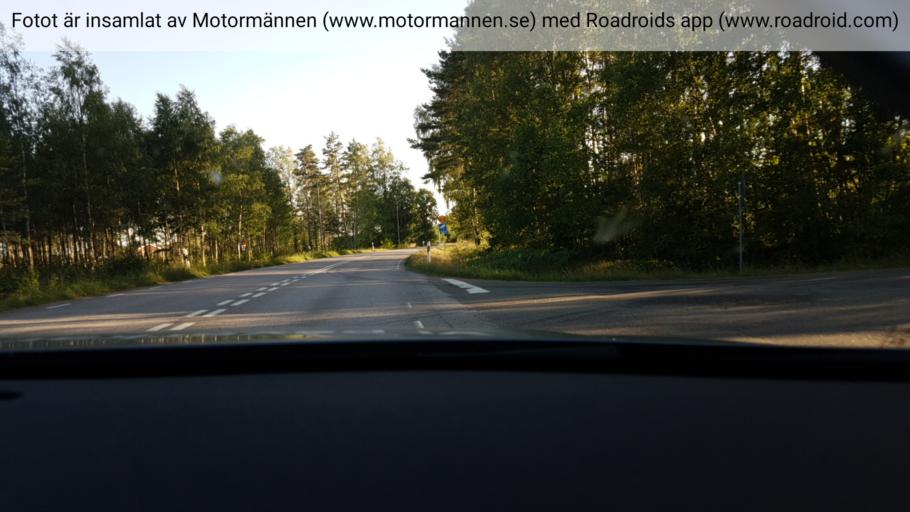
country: SE
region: Vaestra Goetaland
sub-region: Skovde Kommun
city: Stopen
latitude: 58.4371
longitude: 13.9329
